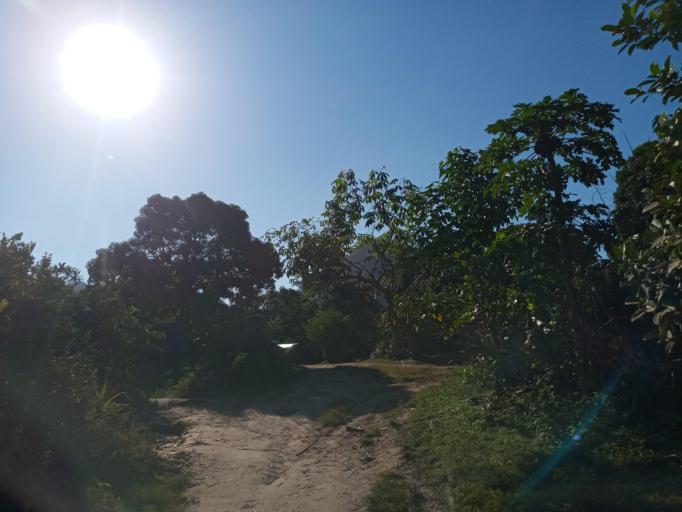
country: MG
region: Anosy
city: Fort Dauphin
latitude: -24.8256
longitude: 47.0446
